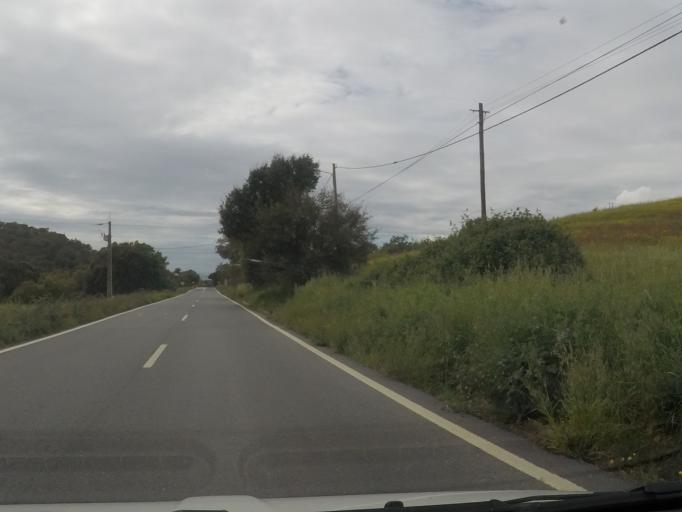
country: PT
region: Setubal
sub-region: Sines
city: Porto Covo
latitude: 37.8667
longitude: -8.7325
